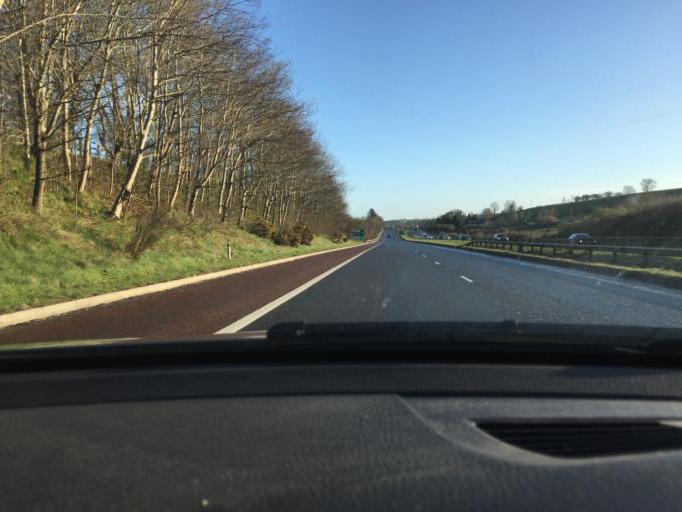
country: GB
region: Northern Ireland
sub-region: Newry and Mourne District
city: Newry
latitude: 54.2650
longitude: -6.3143
